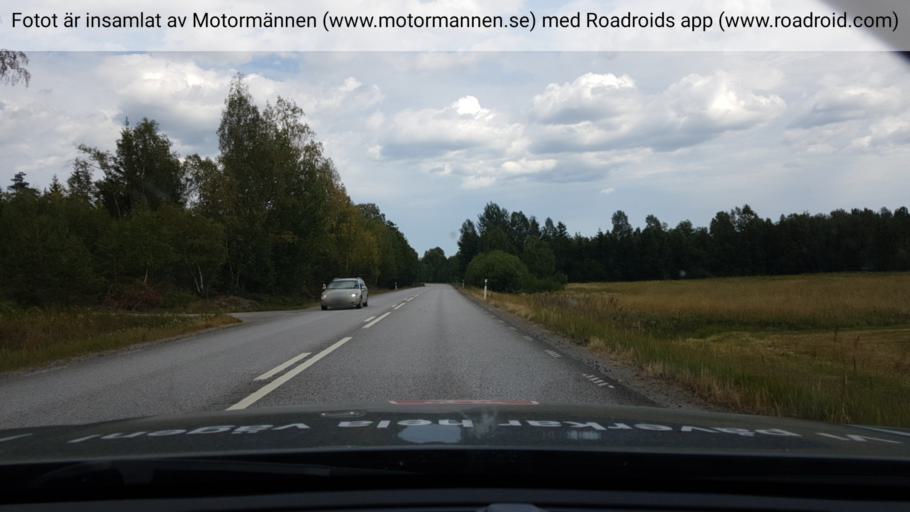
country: SE
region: Uppsala
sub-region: Enkopings Kommun
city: Orsundsbro
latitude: 59.8907
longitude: 17.1689
